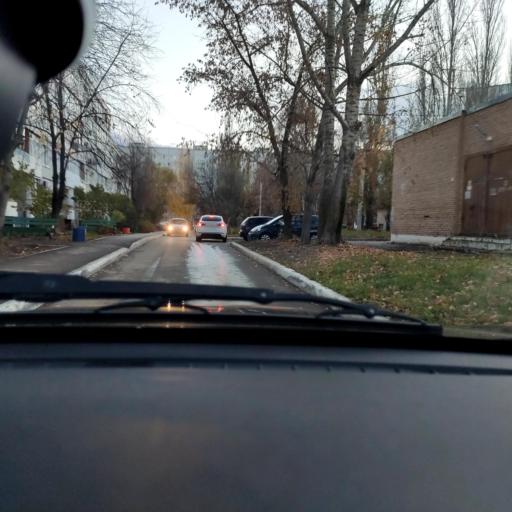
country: RU
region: Samara
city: Tol'yatti
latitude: 53.5087
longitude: 49.4410
